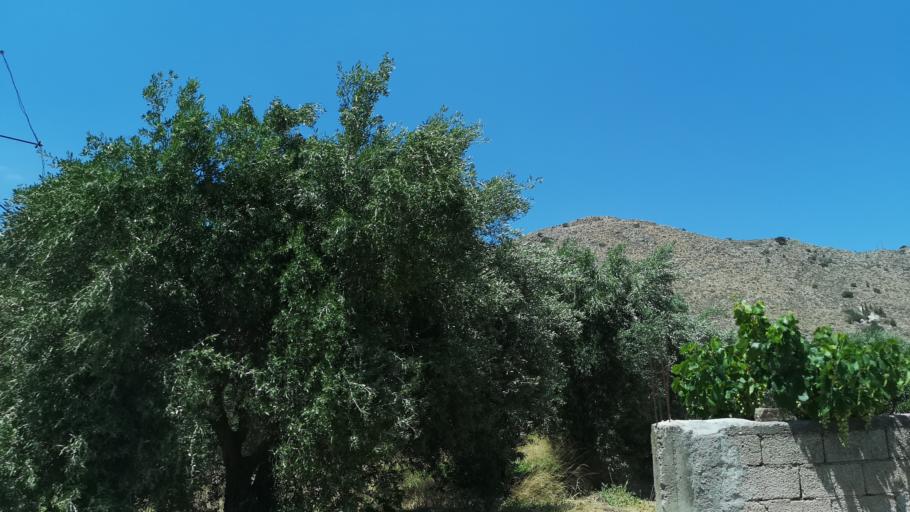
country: GR
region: Crete
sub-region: Nomos Lasithiou
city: Neapoli
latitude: 35.2461
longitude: 25.6334
